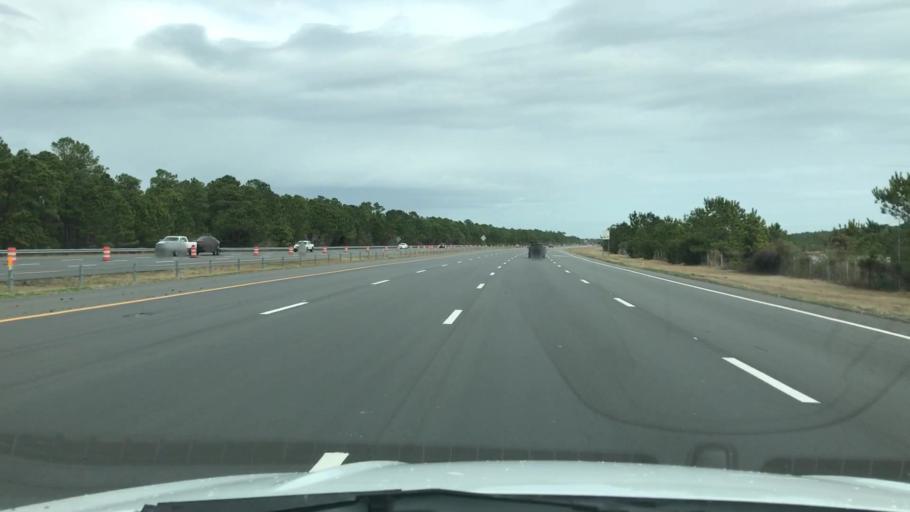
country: US
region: South Carolina
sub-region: Horry County
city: Socastee
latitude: 33.7098
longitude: -79.0083
